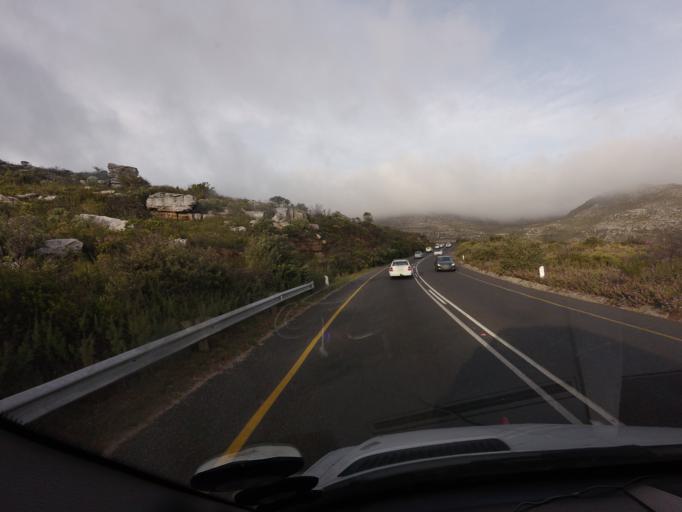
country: ZA
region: Western Cape
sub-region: City of Cape Town
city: Bergvliet
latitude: -34.1007
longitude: 18.4192
